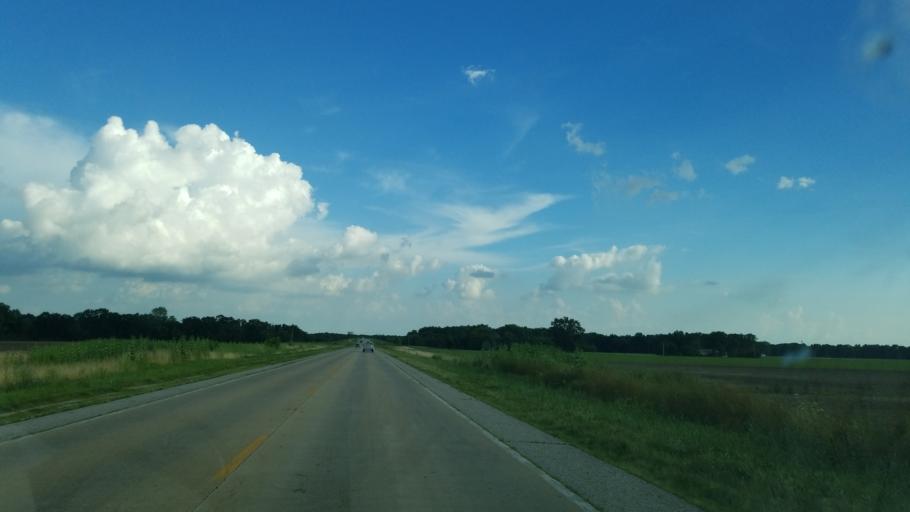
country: US
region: Illinois
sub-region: Marion County
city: Sandoval
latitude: 38.5882
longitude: -89.1084
